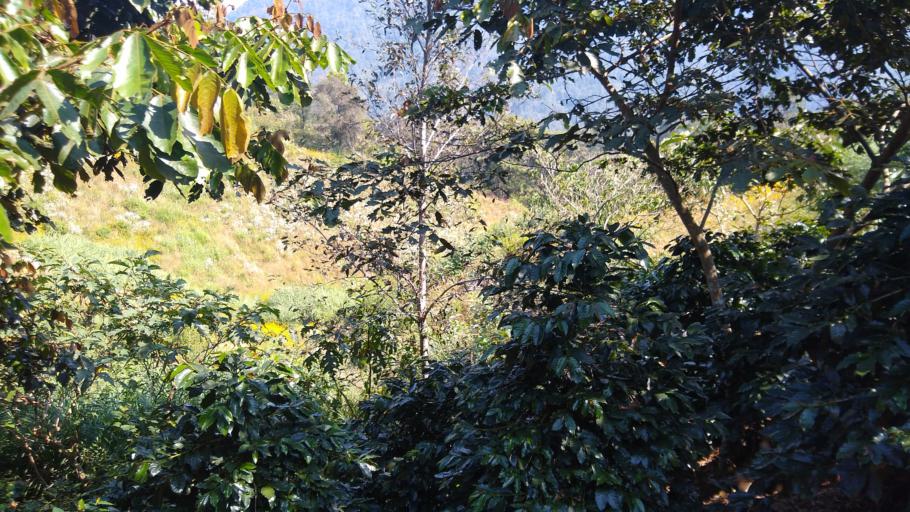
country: MX
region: Puebla
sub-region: Tepetzintla
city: Tlamanca de Hernandez
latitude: 19.9472
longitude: -97.7852
